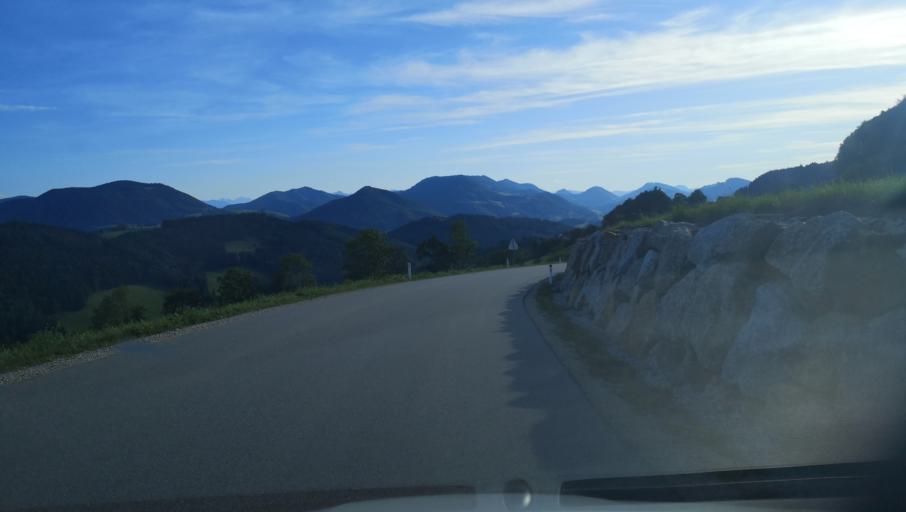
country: AT
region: Lower Austria
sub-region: Waidhofen an der Ybbs Stadt
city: Waidhofen an der Ybbs
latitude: 47.9773
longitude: 14.8298
